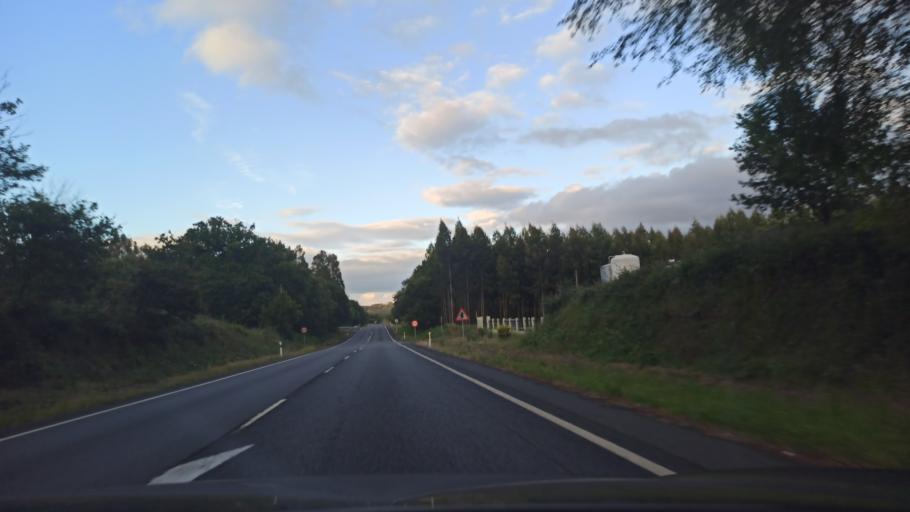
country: ES
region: Galicia
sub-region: Provincia de Pontevedra
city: Rodeiro
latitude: 42.7645
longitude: -8.0012
